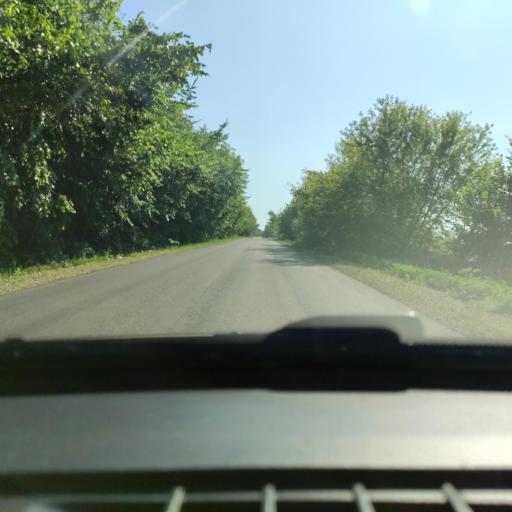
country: RU
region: Voronezj
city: Anna
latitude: 51.6330
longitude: 40.3544
